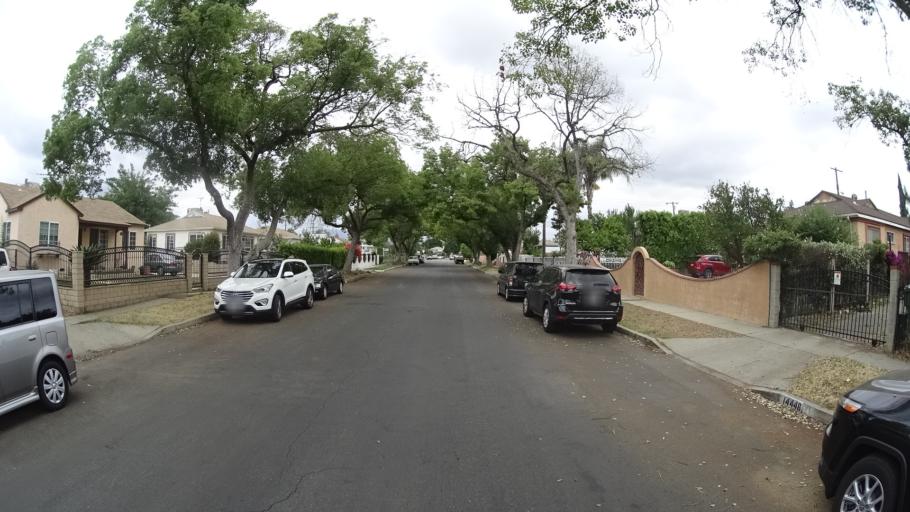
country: US
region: California
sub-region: Los Angeles County
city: San Fernando
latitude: 34.2496
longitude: -118.4477
